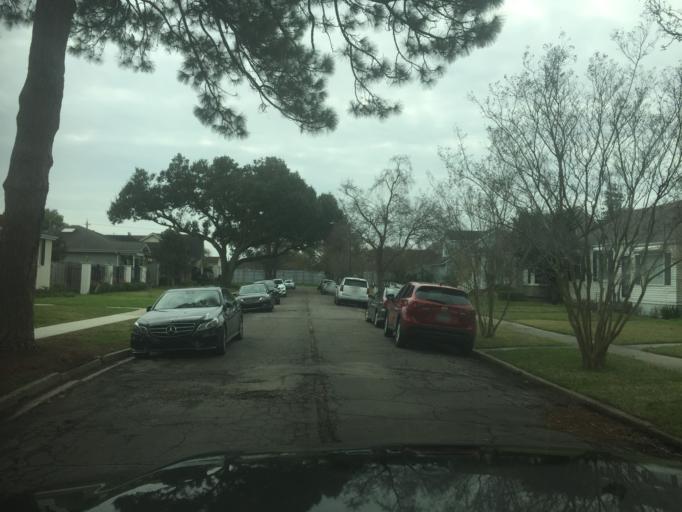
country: US
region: Louisiana
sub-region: Jefferson Parish
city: Metairie
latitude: 29.9964
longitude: -90.1057
